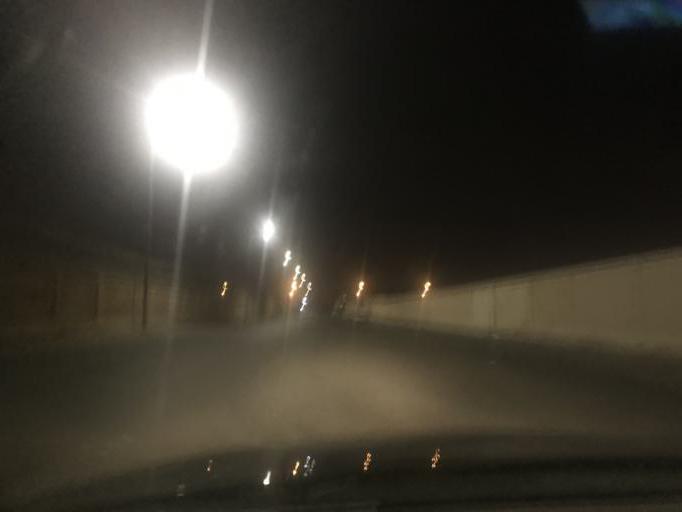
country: SA
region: Ar Riyad
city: Riyadh
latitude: 24.7228
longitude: 46.7845
